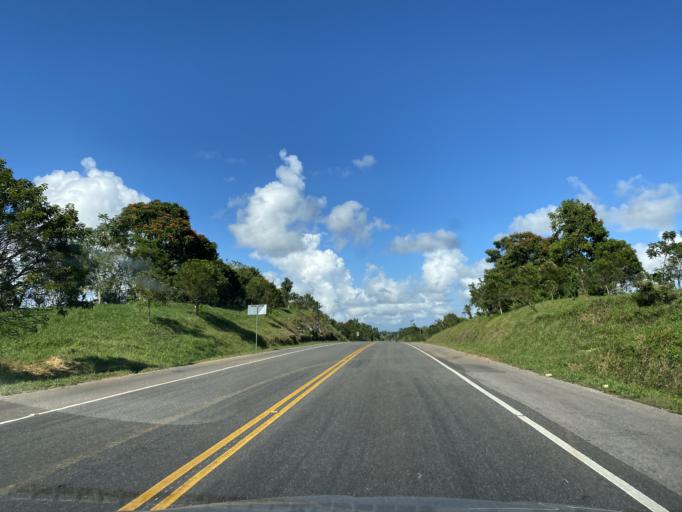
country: DO
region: Monte Plata
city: Majagual
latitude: 19.0133
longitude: -69.8230
